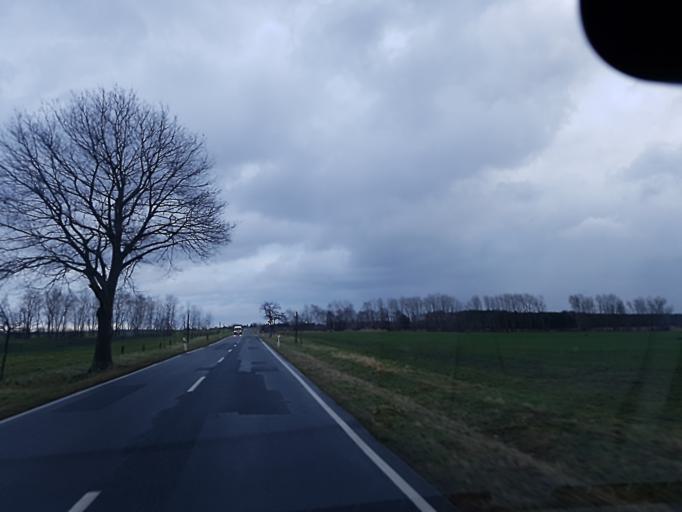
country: DE
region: Brandenburg
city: Hohenleipisch
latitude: 51.5331
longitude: 13.6007
